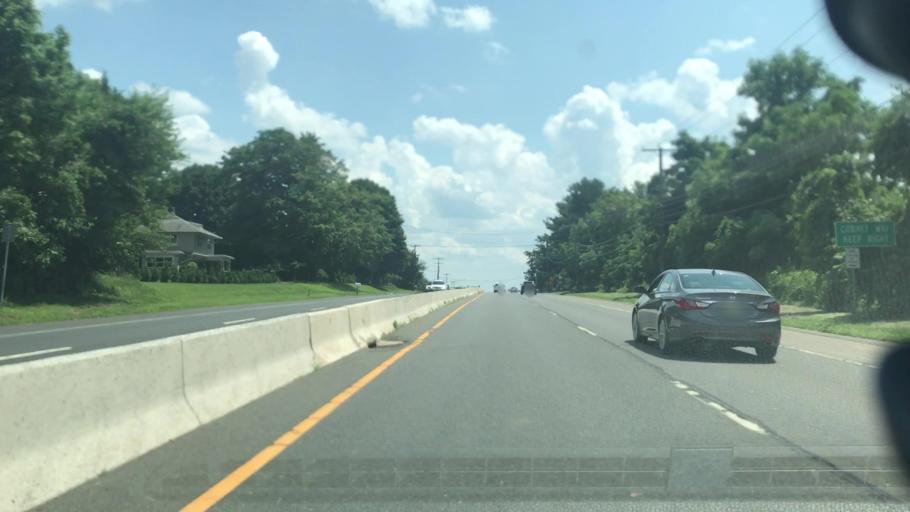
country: US
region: New Jersey
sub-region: Hunterdon County
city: Flemington
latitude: 40.4532
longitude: -74.8594
